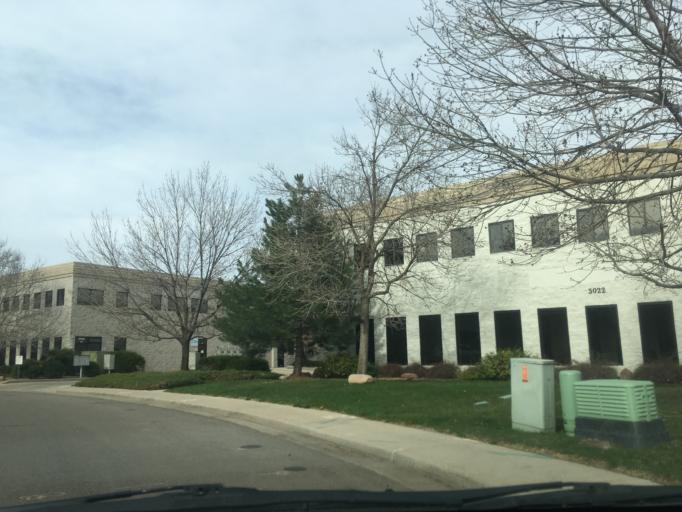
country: US
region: Colorado
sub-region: Boulder County
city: Boulder
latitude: 40.0300
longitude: -105.2268
